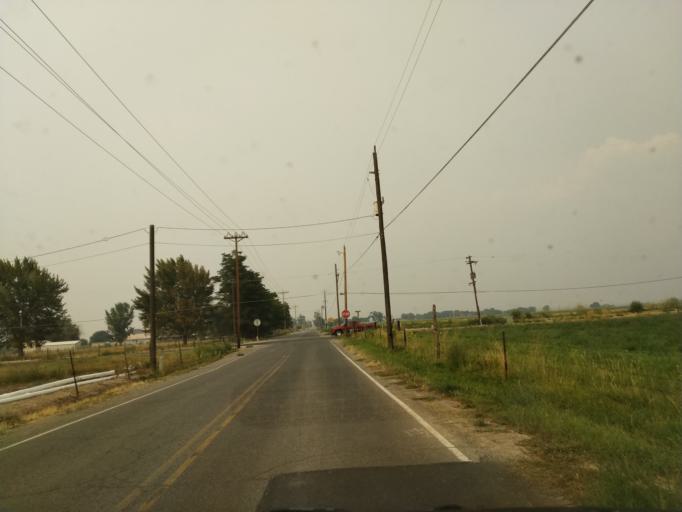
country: US
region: Colorado
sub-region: Mesa County
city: Fruitvale
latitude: 39.0405
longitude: -108.4967
